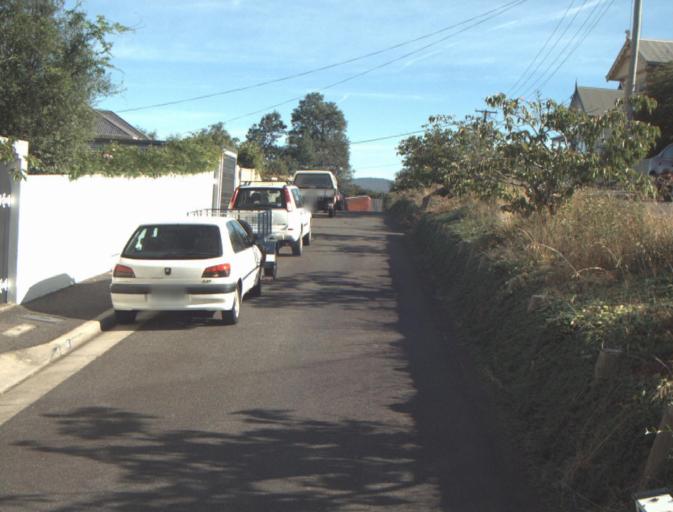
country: AU
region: Tasmania
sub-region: Launceston
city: East Launceston
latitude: -41.4383
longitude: 147.1527
